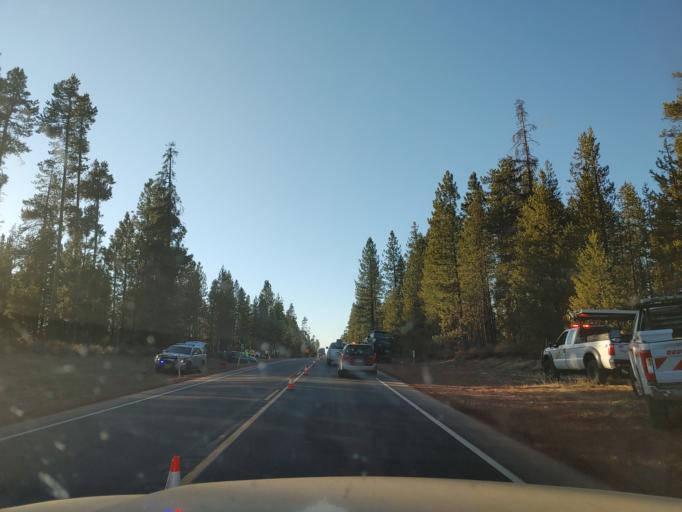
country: US
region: Oregon
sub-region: Deschutes County
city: La Pine
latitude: 43.3819
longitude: -121.8026
